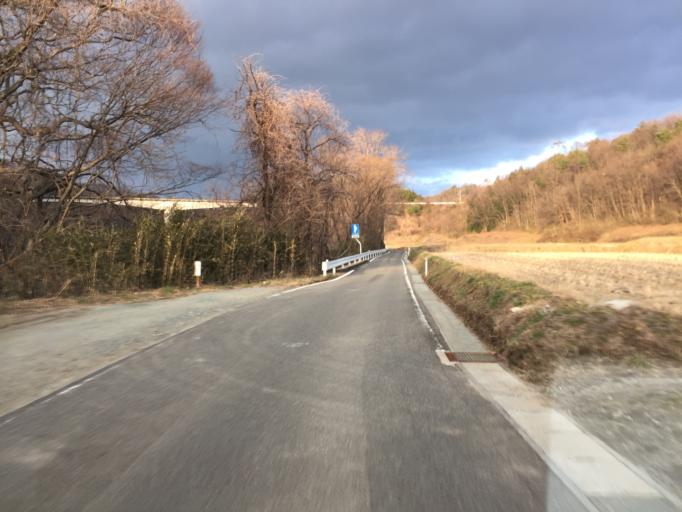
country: JP
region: Fukushima
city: Motomiya
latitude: 37.5324
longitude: 140.4149
